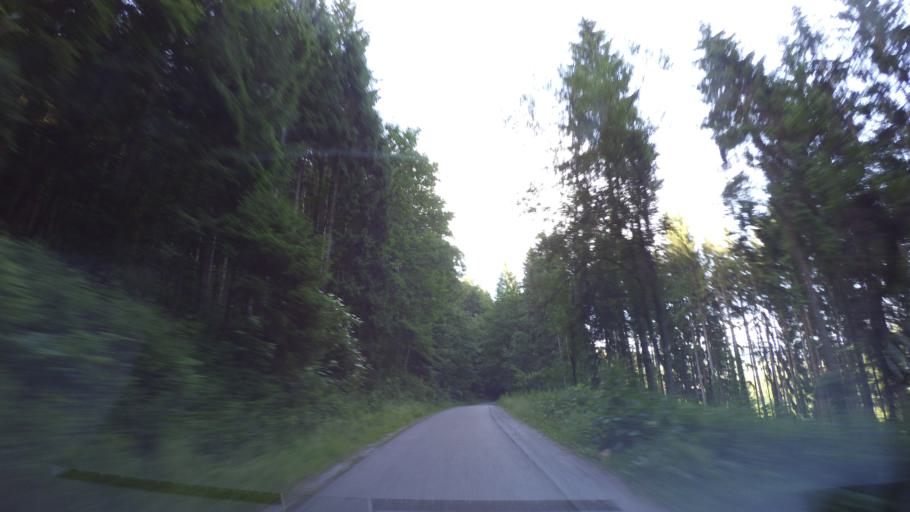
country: DE
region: Baden-Wuerttemberg
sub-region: Regierungsbezirk Stuttgart
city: Fichtenberg
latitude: 48.9790
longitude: 9.6981
